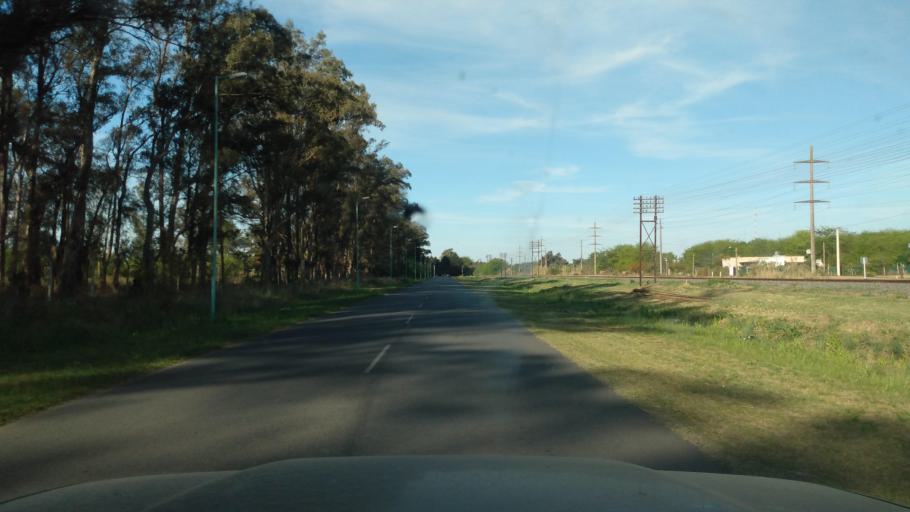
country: AR
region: Buenos Aires
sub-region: Partido de Lujan
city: Lujan
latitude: -34.5869
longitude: -59.1331
